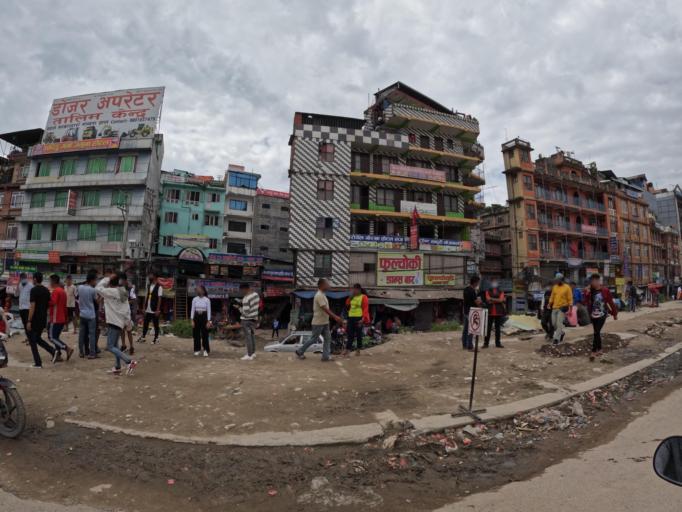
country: NP
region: Central Region
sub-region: Bagmati Zone
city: Kathmandu
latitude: 27.7353
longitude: 85.3080
